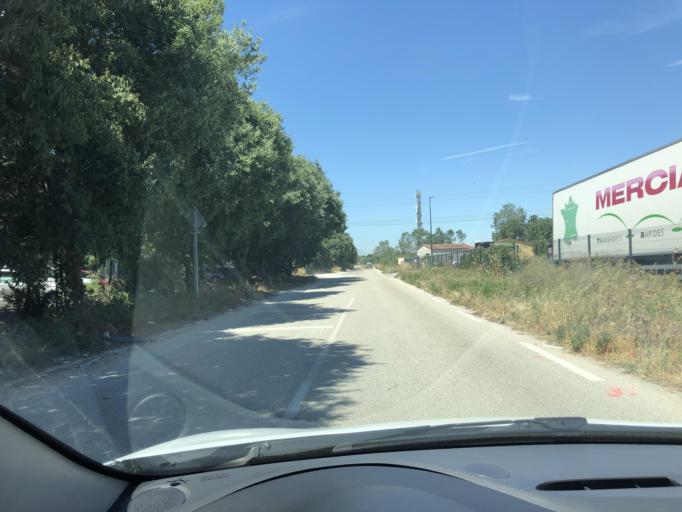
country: FR
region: Provence-Alpes-Cote d'Azur
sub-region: Departement des Bouches-du-Rhone
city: Chateaurenard
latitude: 43.8995
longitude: 4.8749
